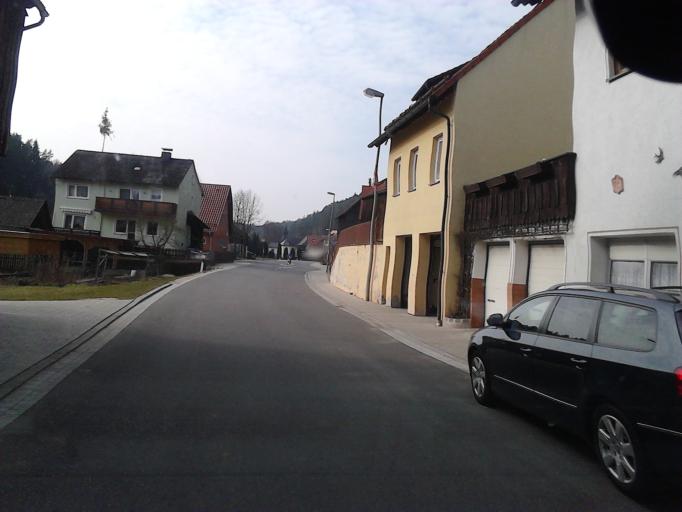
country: DE
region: Bavaria
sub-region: Upper Franconia
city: Stadelhofen
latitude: 49.9649
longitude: 11.2018
